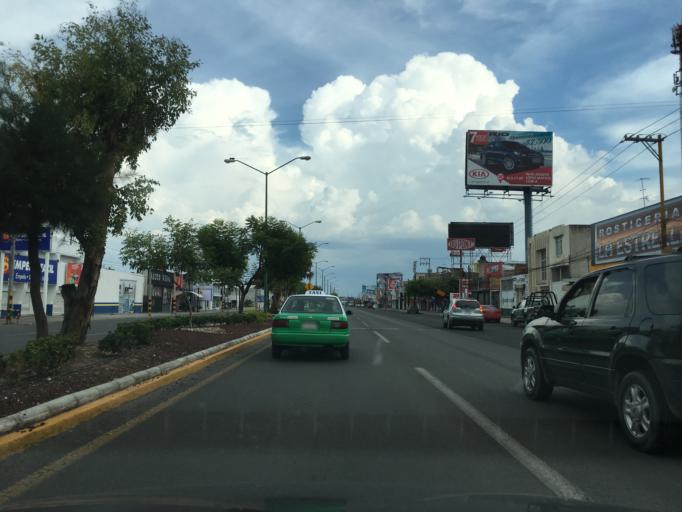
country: MX
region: Guanajuato
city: Celaya
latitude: 20.5427
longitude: -100.8208
